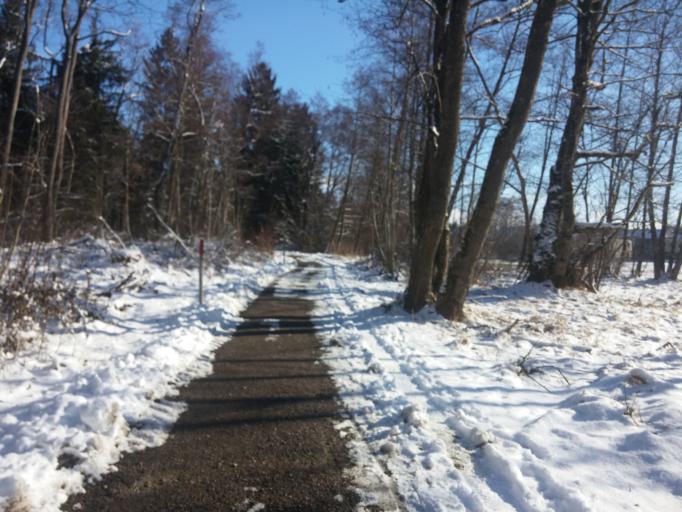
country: DE
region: Baden-Wuerttemberg
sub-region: Tuebingen Region
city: Leutkirch im Allgau
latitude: 47.8326
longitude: 10.0346
